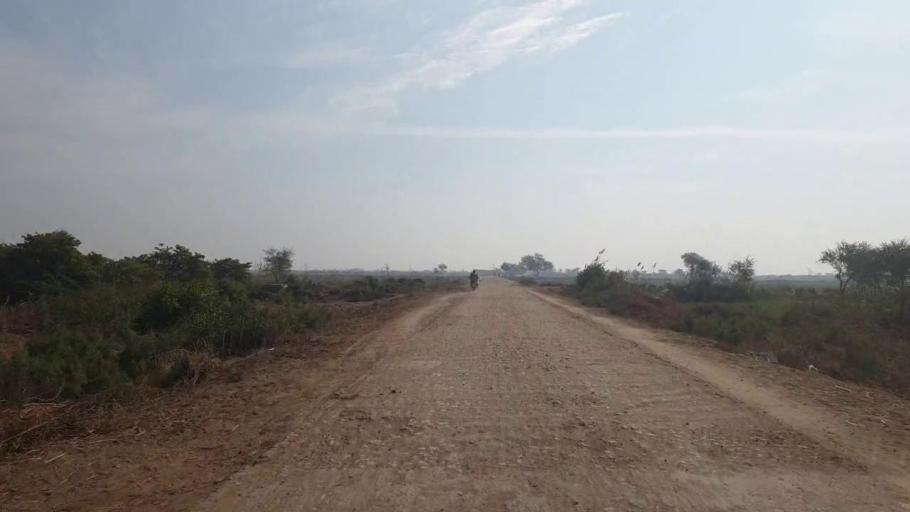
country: PK
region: Sindh
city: Mirwah Gorchani
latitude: 25.3689
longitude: 69.1814
